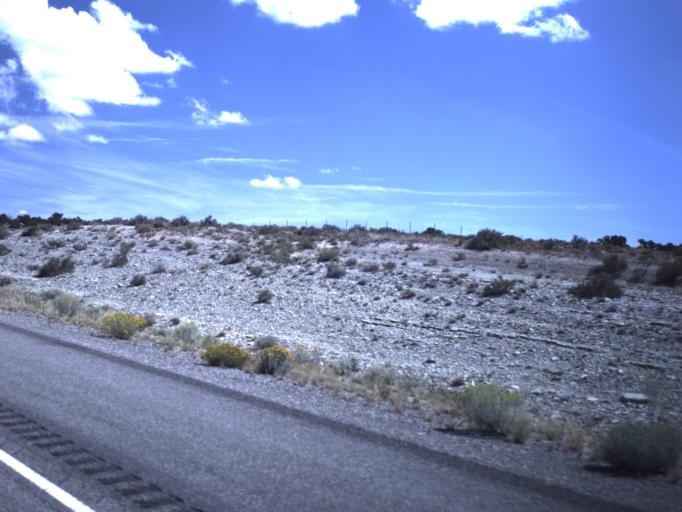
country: US
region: Utah
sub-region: Emery County
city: Ferron
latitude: 38.8413
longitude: -110.9603
